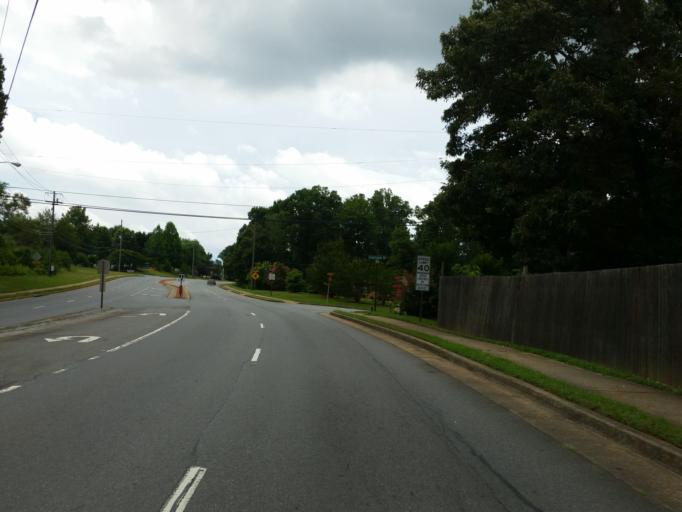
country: US
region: Georgia
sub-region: Cobb County
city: Kennesaw
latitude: 34.0765
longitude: -84.5886
